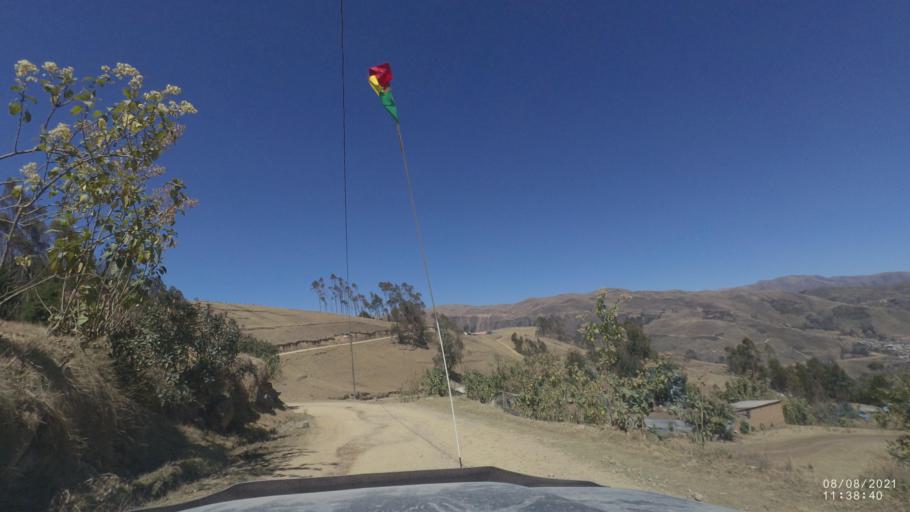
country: BO
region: Cochabamba
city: Colchani
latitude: -16.7905
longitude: -66.6509
